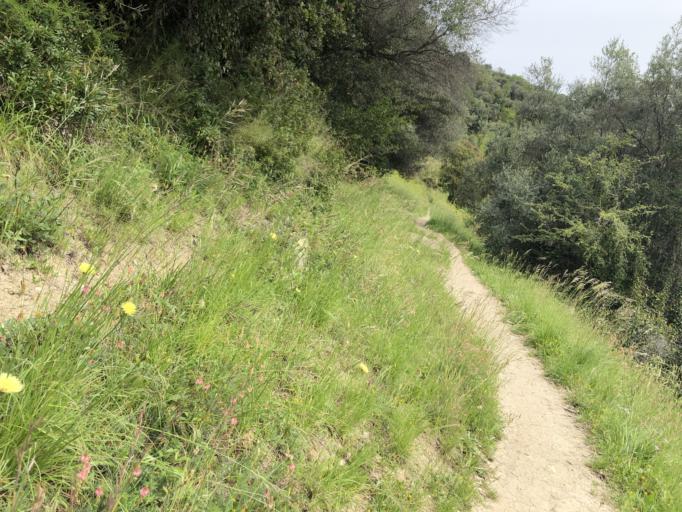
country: FR
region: Provence-Alpes-Cote d'Azur
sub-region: Departement des Alpes-Maritimes
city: Saint-Andre-de-la-Roche
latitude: 43.7219
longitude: 7.2980
